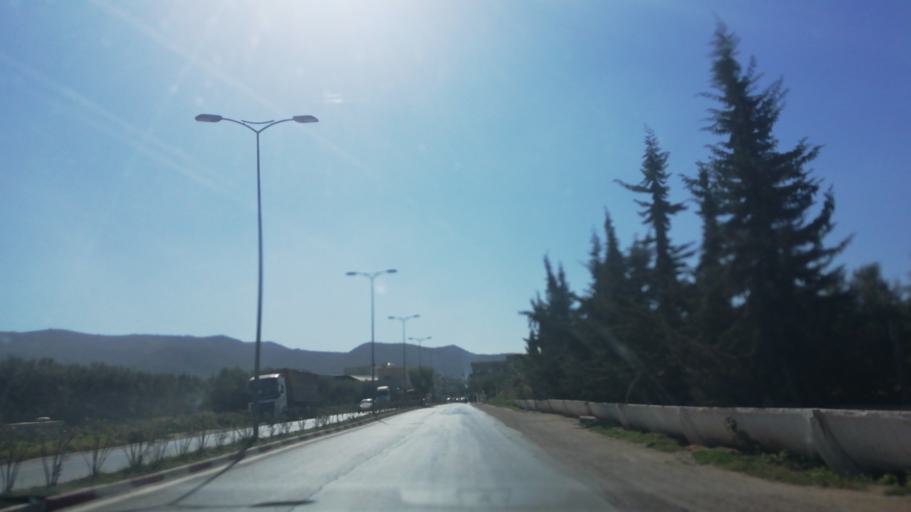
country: DZ
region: Mascara
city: Sig
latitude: 35.5318
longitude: -0.2026
